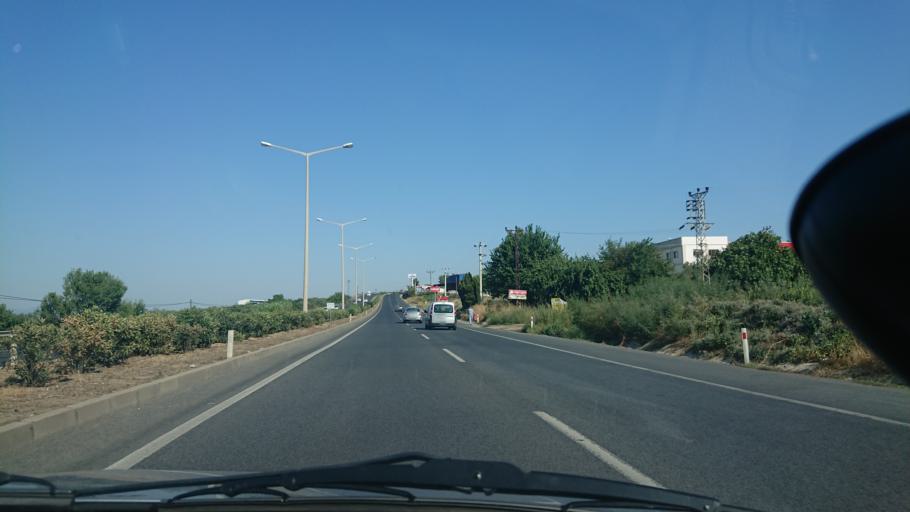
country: TR
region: Manisa
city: Turgutlu
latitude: 38.4953
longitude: 27.7715
